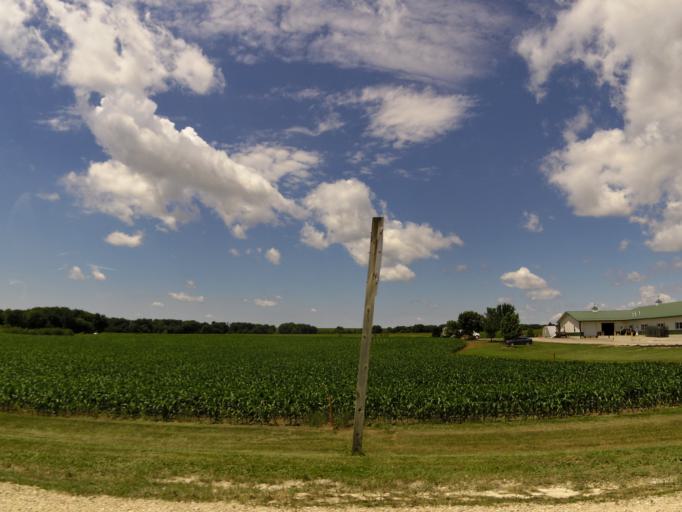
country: US
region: Iowa
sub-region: Fayette County
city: Oelwein
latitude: 42.7123
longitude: -91.9131
